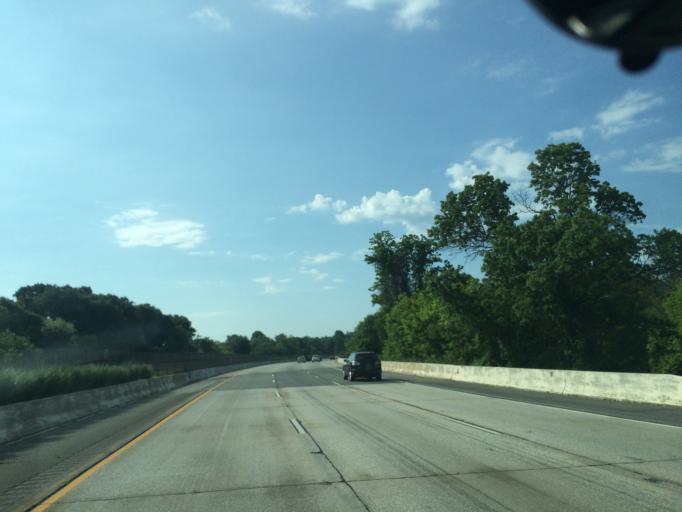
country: US
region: Maryland
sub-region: Baltimore County
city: Garrison
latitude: 39.4028
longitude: -76.7666
